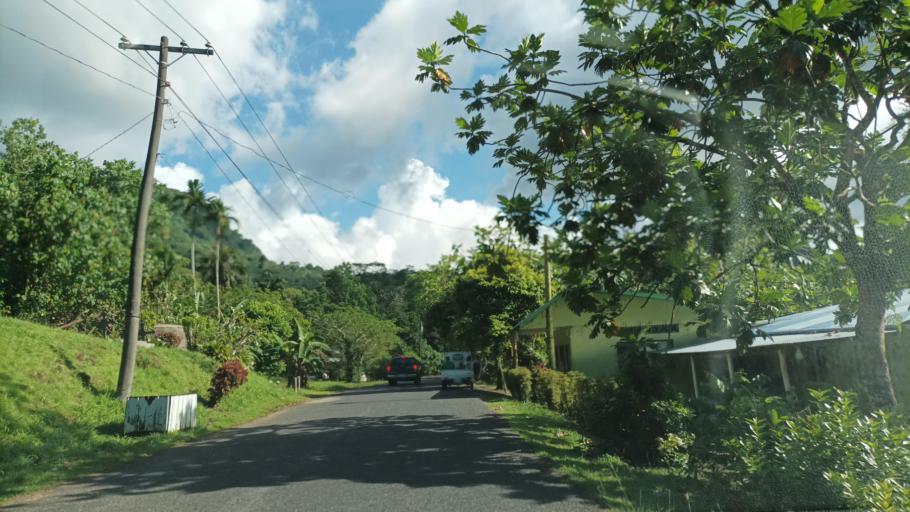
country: FM
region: Pohnpei
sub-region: Kolonia Municipality
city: Kolonia
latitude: 6.9579
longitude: 158.2491
